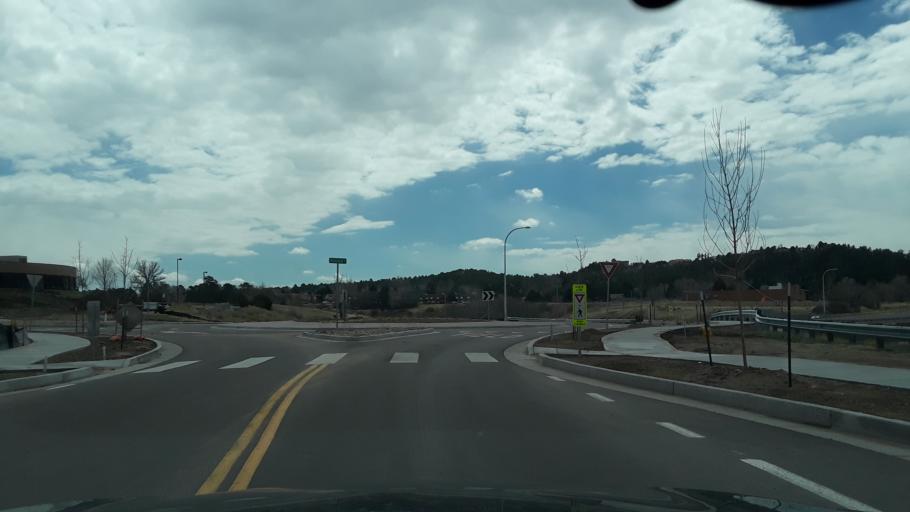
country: US
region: Colorado
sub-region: El Paso County
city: Air Force Academy
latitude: 38.9294
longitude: -104.8101
